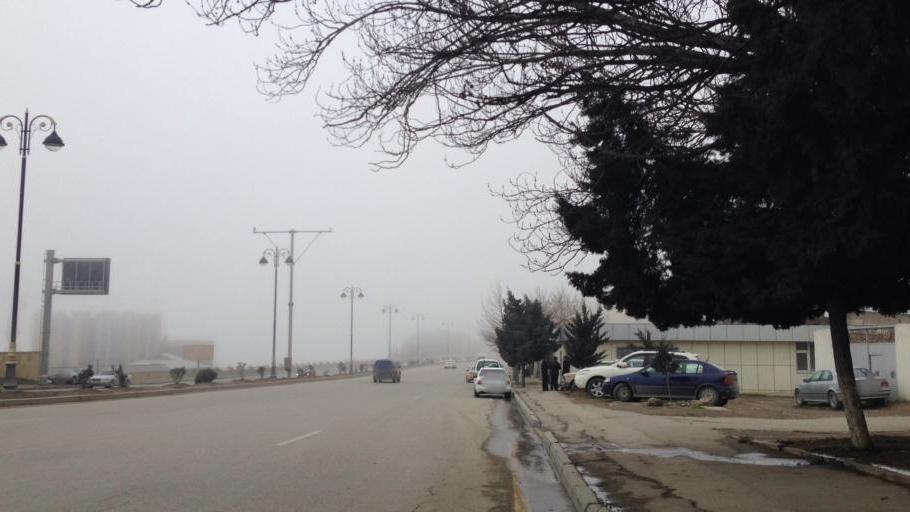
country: AZ
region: Baki
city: Qaracuxur
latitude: 40.3536
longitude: 49.9565
